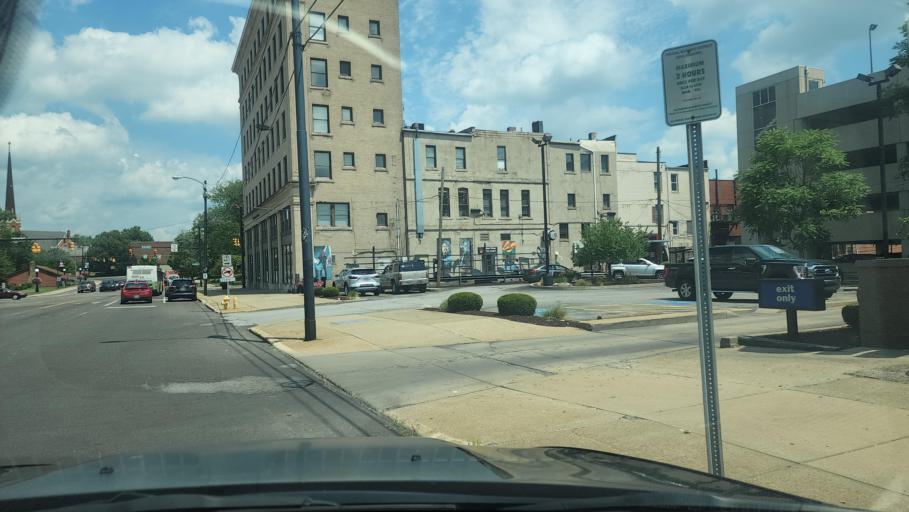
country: US
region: Ohio
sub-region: Trumbull County
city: Warren
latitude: 41.2353
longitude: -80.8199
